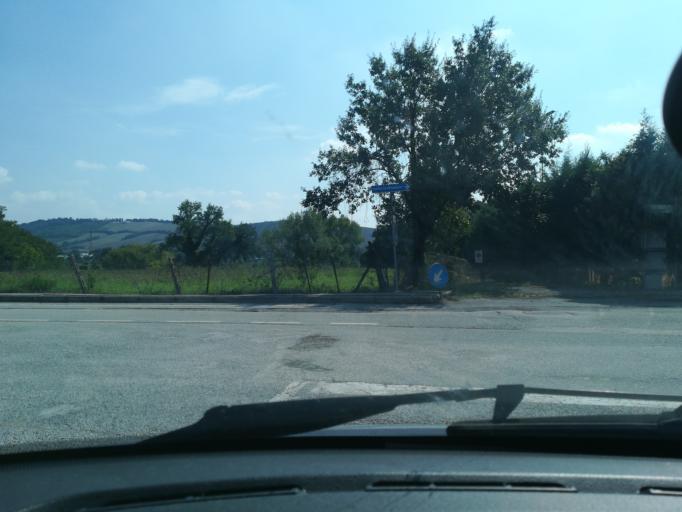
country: IT
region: The Marches
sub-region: Provincia di Macerata
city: Casette Verdini
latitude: 43.2500
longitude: 13.4063
